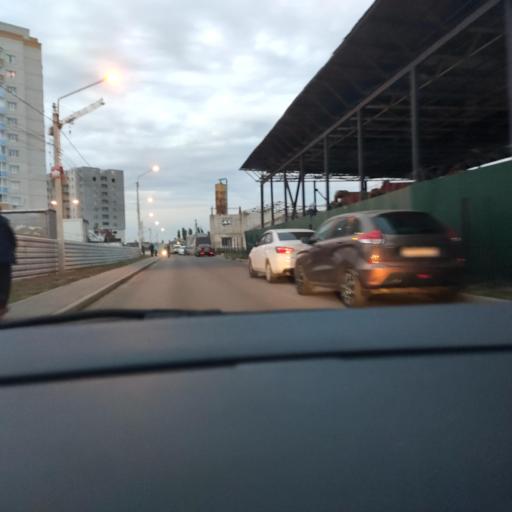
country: RU
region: Voronezj
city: Podgornoye
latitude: 51.7207
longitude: 39.1416
